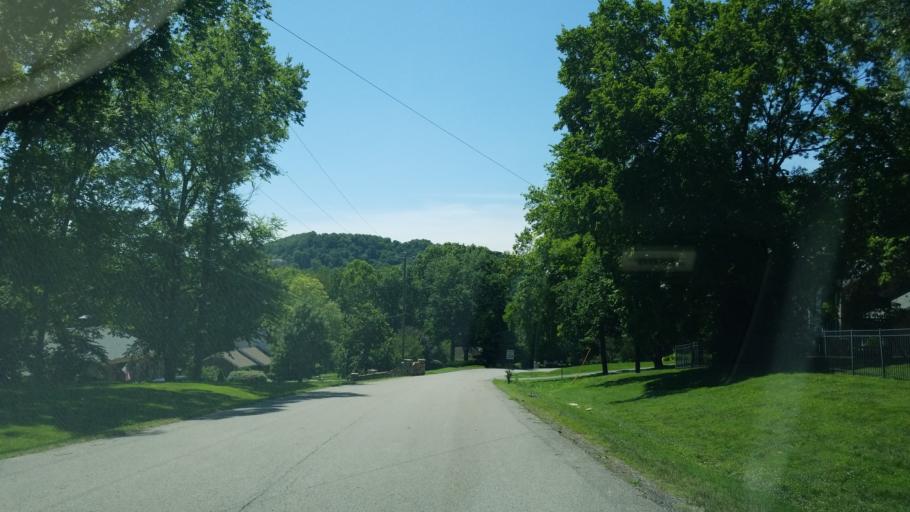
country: US
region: Tennessee
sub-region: Williamson County
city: Brentwood
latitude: 36.0562
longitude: -86.8104
